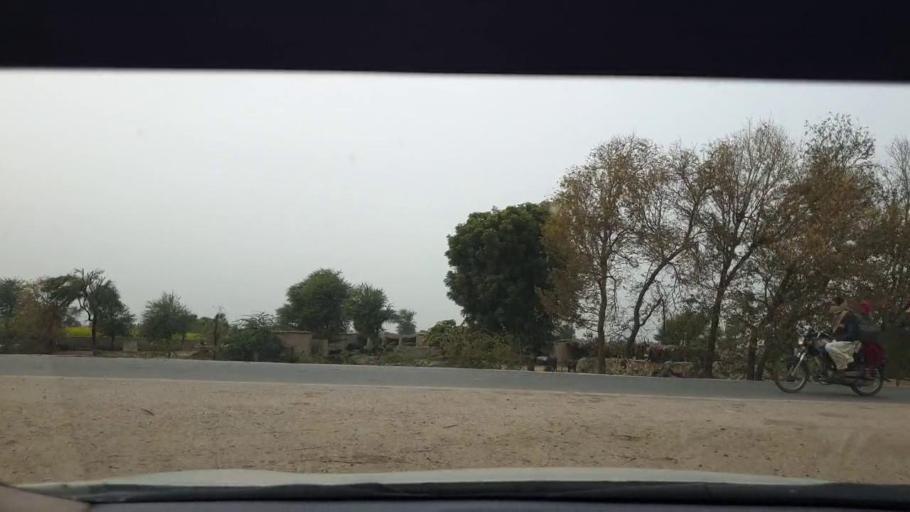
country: PK
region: Sindh
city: Berani
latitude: 25.8869
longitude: 68.8073
